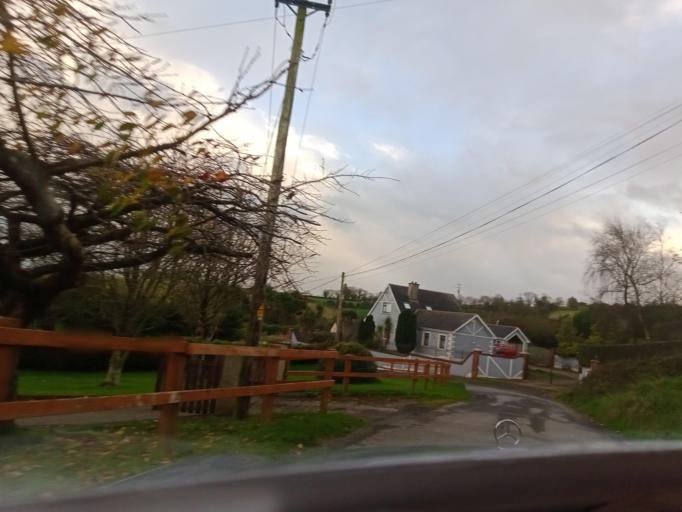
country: IE
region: Leinster
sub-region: Loch Garman
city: New Ross
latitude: 52.3468
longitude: -7.0284
